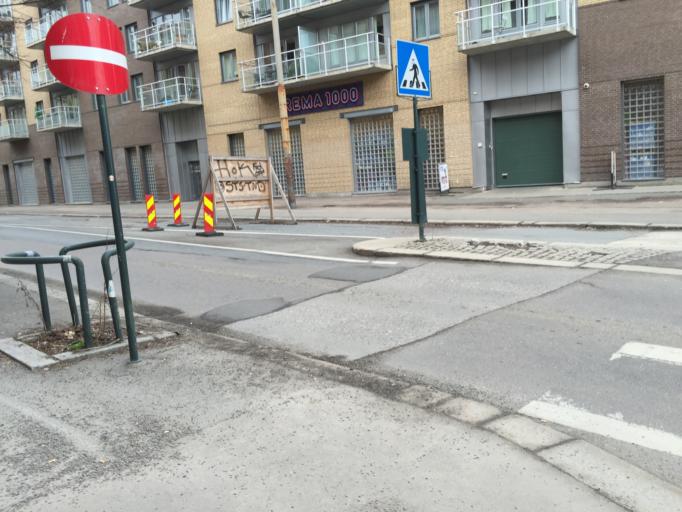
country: NO
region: Oslo
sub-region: Oslo
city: Oslo
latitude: 59.9177
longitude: 10.7625
